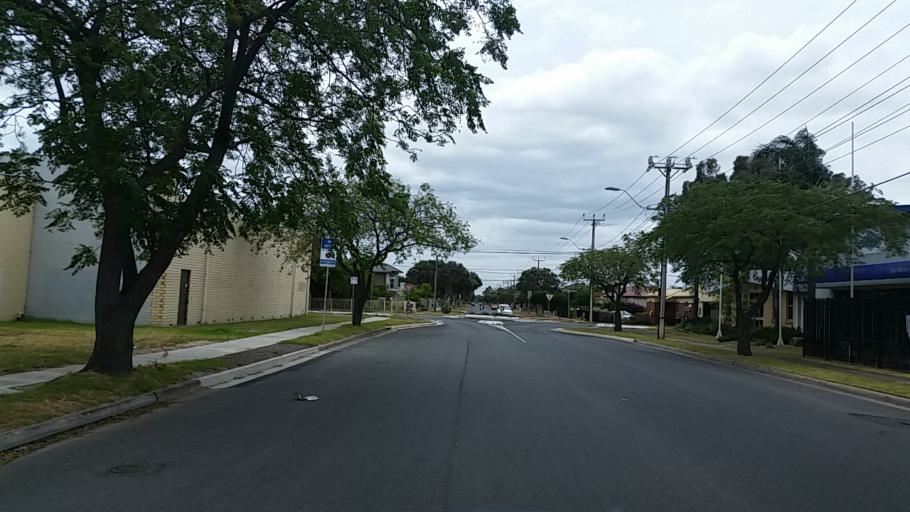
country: AU
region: South Australia
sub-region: Charles Sturt
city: Woodville North
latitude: -34.8727
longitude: 138.5545
